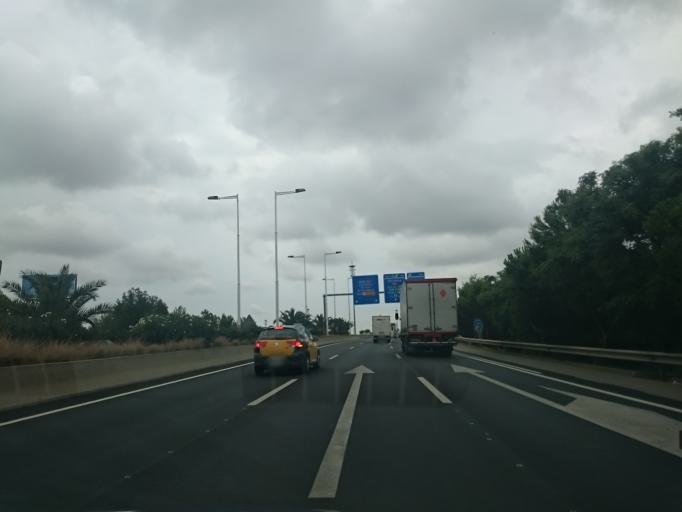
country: ES
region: Catalonia
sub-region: Provincia de Barcelona
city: Cornella de Llobregat
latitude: 41.3493
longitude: 2.0921
